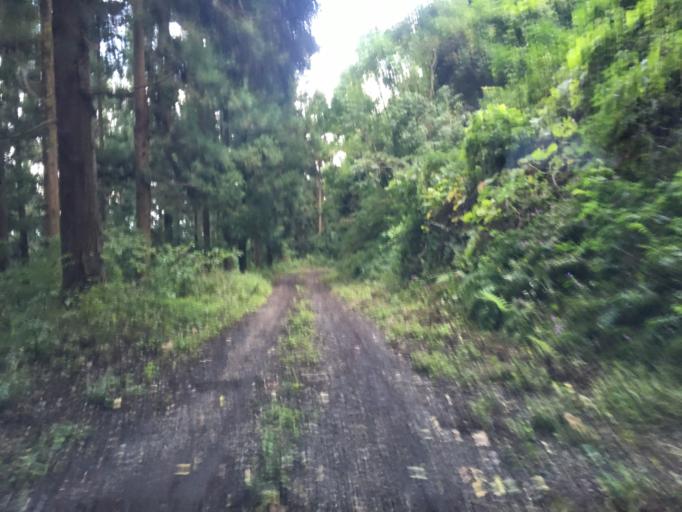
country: JP
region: Fukushima
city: Yanagawamachi-saiwaicho
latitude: 37.9025
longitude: 140.5451
